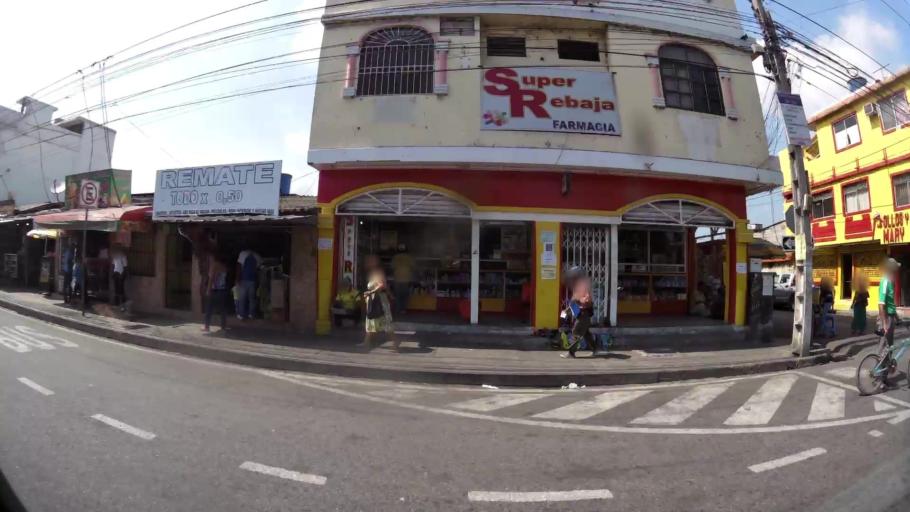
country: EC
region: Guayas
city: Eloy Alfaro
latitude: -2.1641
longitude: -79.8440
